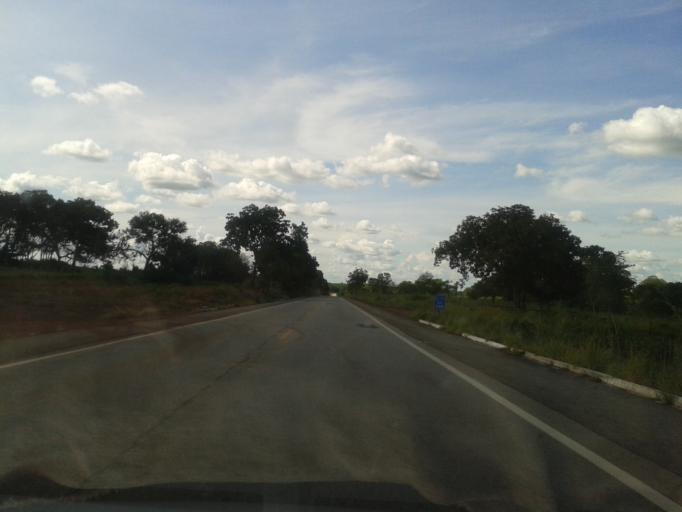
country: BR
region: Goias
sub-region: Mozarlandia
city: Mozarlandia
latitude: -15.2254
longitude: -50.5243
